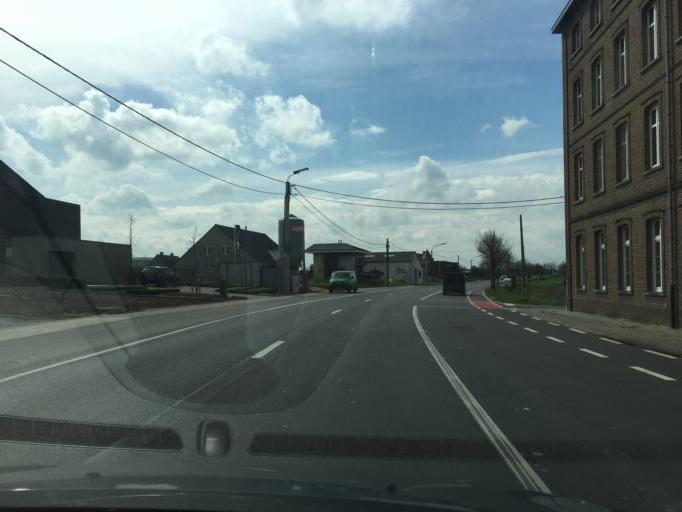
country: BE
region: Flanders
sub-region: Provincie West-Vlaanderen
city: Tielt
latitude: 51.0110
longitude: 3.3609
